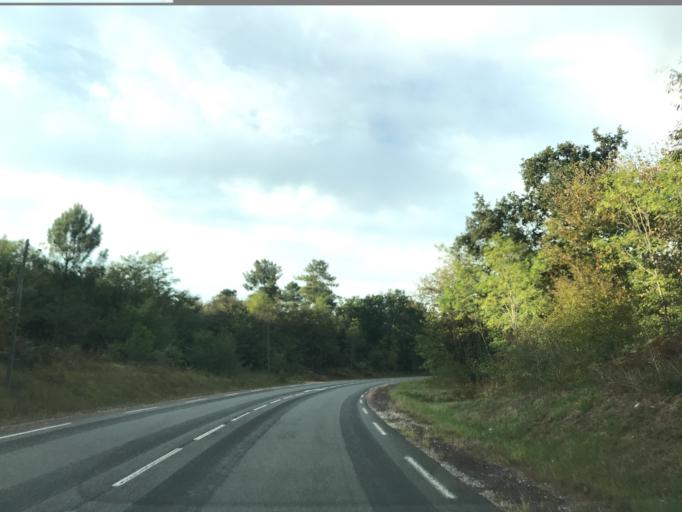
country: FR
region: Aquitaine
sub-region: Departement de la Dordogne
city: Riberac
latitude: 45.1875
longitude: 0.3761
